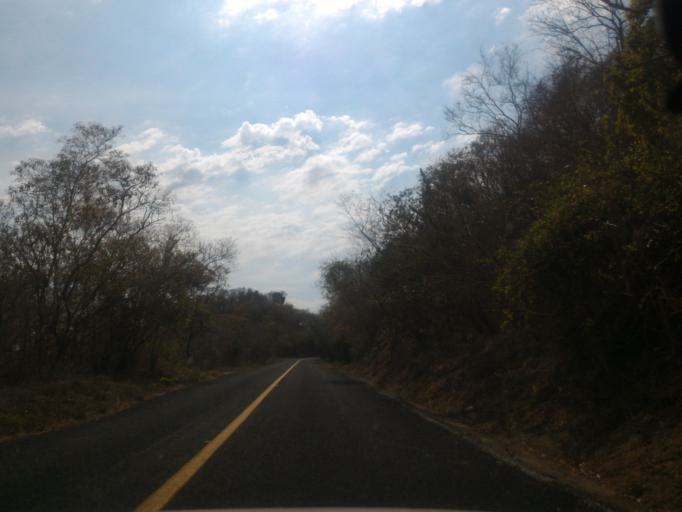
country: MX
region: Michoacan
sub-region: Coalcoman de Vazquez Pallares
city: Coalcoman de Vazquez Pallares
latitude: 18.2819
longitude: -103.3732
